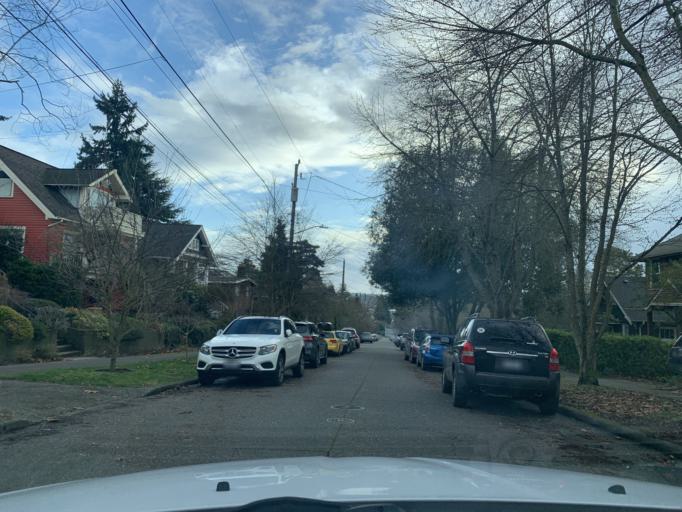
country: US
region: Washington
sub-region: King County
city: Seattle
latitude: 47.6712
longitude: -122.2973
